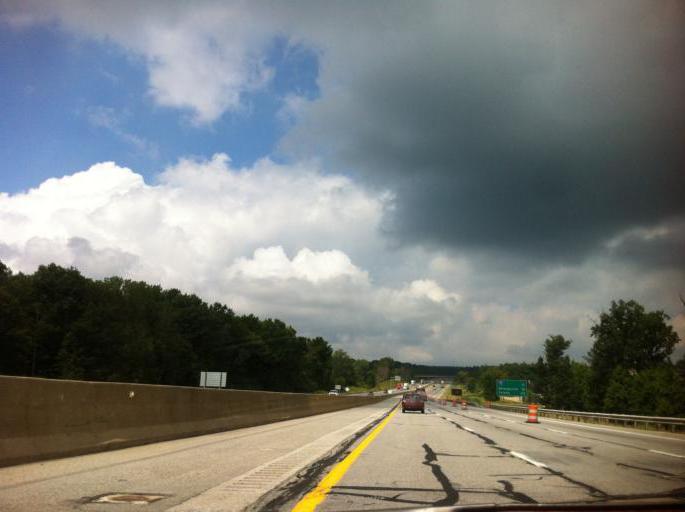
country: US
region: Ohio
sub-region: Summit County
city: Richfield
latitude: 41.2765
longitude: -81.6387
